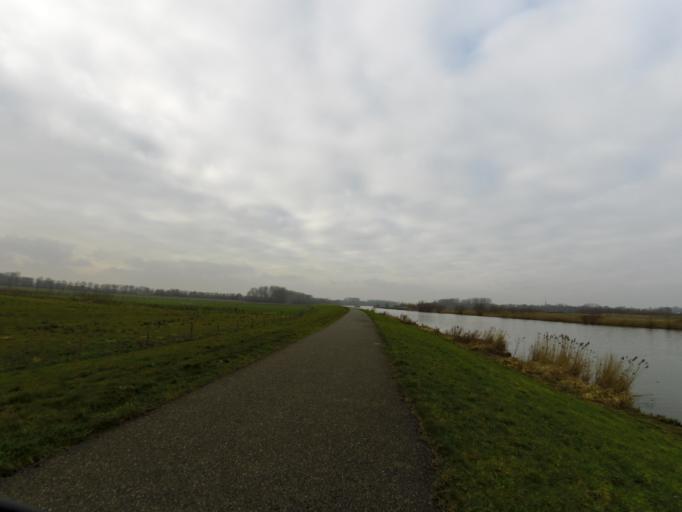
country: NL
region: Gelderland
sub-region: Gemeente Doesburg
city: Doesburg
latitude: 51.9997
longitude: 6.1679
